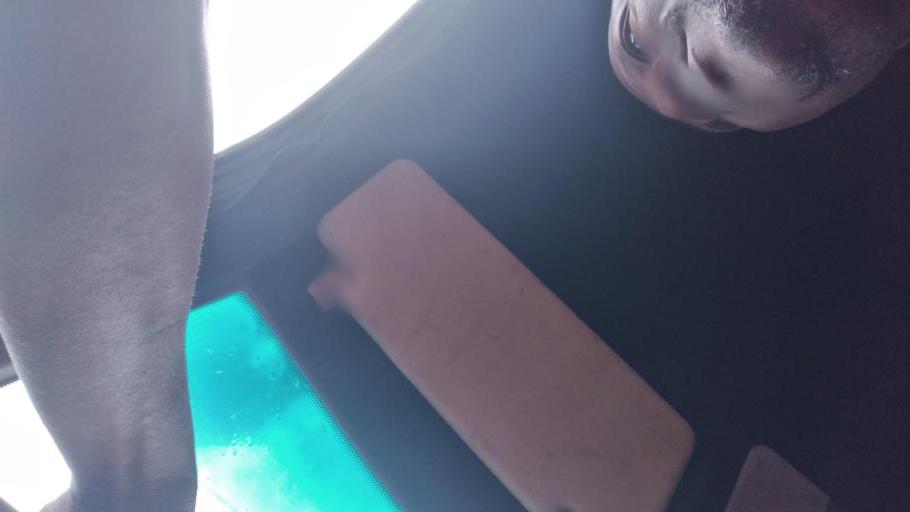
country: ML
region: Bamako
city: Bamako
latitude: 12.6515
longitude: -7.9940
